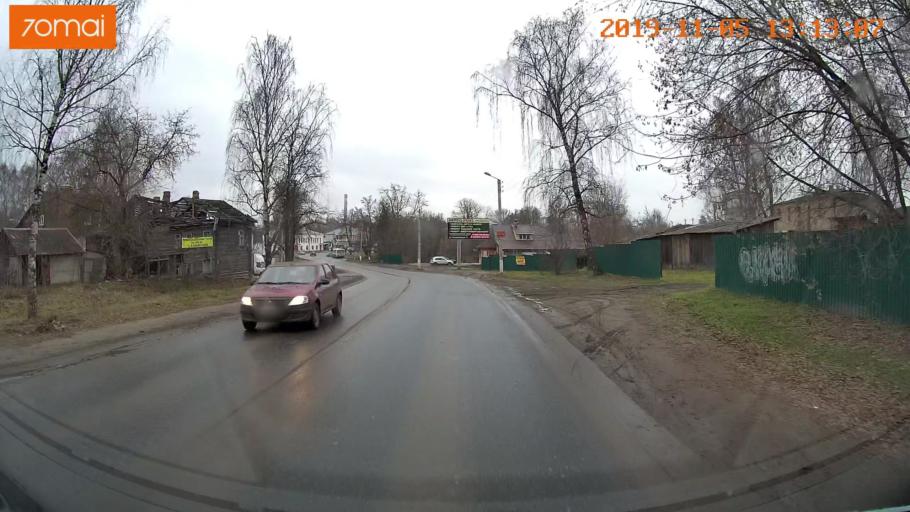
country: RU
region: Ivanovo
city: Shuya
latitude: 56.8530
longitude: 41.3532
